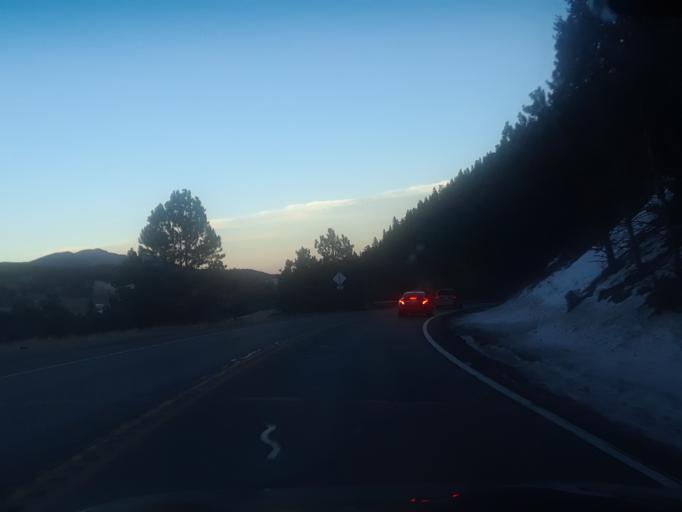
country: US
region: Colorado
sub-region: Clear Creek County
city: Georgetown
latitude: 39.4486
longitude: -105.6215
